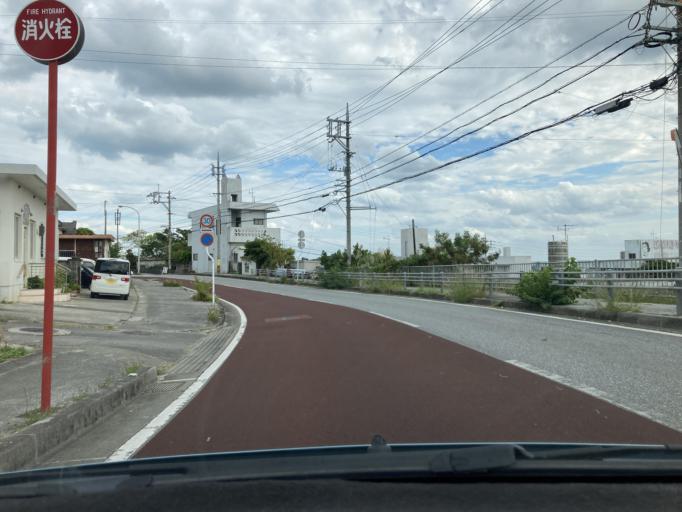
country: JP
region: Okinawa
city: Gushikawa
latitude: 26.3487
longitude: 127.8436
